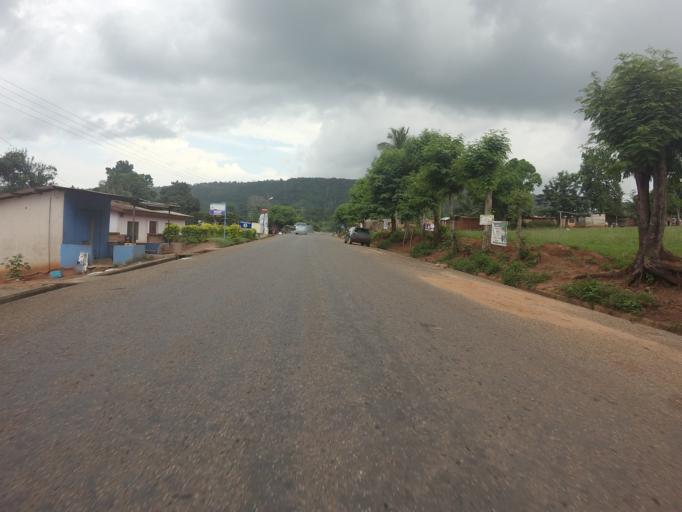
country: GH
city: Akropong
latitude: 5.9590
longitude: -0.1308
